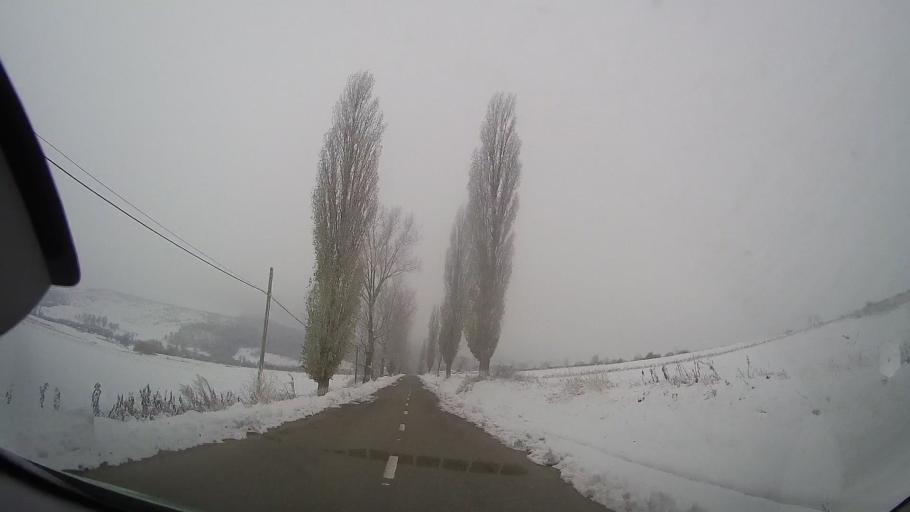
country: RO
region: Neamt
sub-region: Comuna Bozieni
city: Bozieni
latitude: 46.8419
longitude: 27.1684
